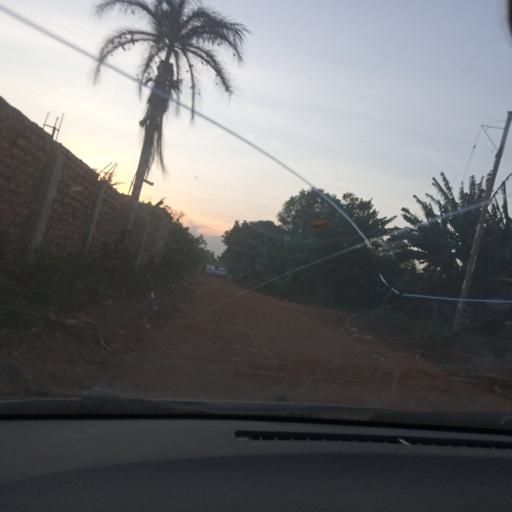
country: UG
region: Central Region
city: Masaka
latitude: -0.3147
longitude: 31.7693
